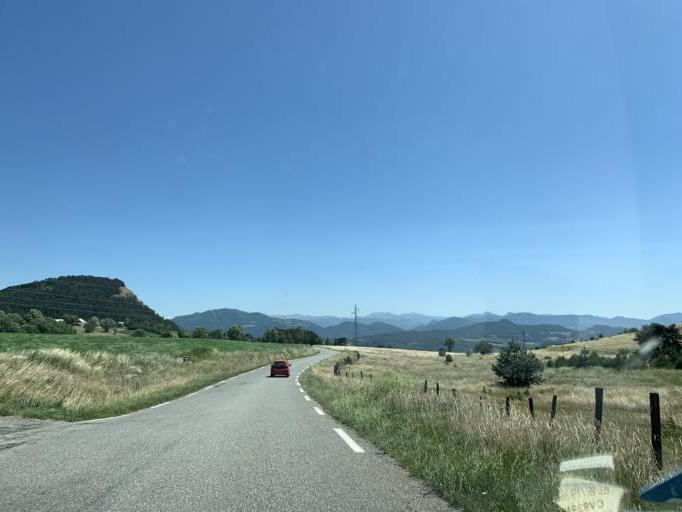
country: FR
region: Provence-Alpes-Cote d'Azur
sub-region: Departement des Hautes-Alpes
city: Gap
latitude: 44.6094
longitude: 6.1406
